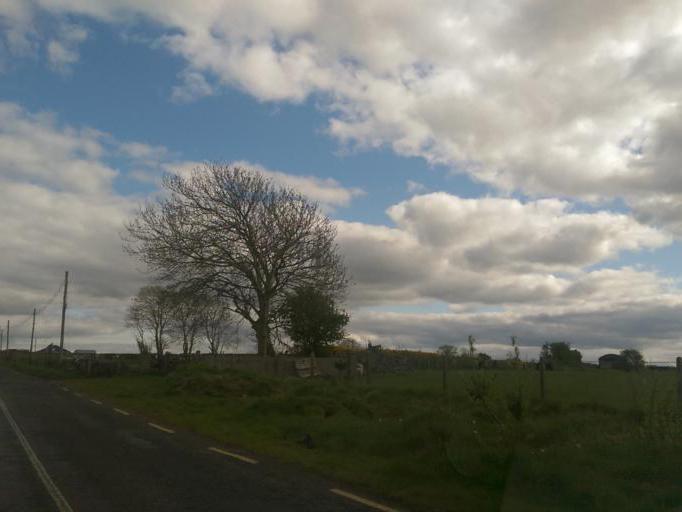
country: IE
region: Connaught
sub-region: County Galway
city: Loughrea
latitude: 53.4214
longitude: -8.5277
